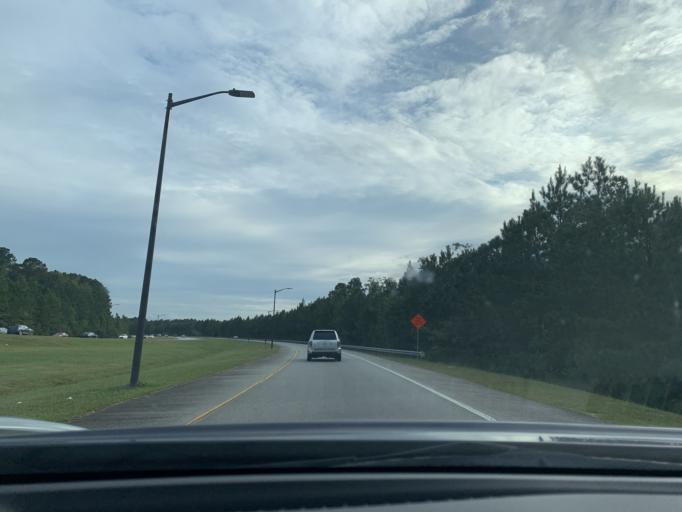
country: US
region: Georgia
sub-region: Chatham County
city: Pooler
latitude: 32.1199
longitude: -81.2694
